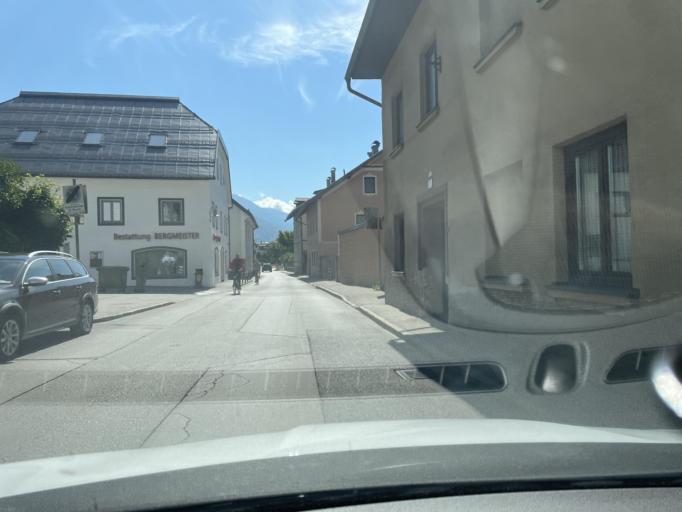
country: AT
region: Tyrol
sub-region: Politischer Bezirk Lienz
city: Lienz
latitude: 46.8329
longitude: 12.7684
